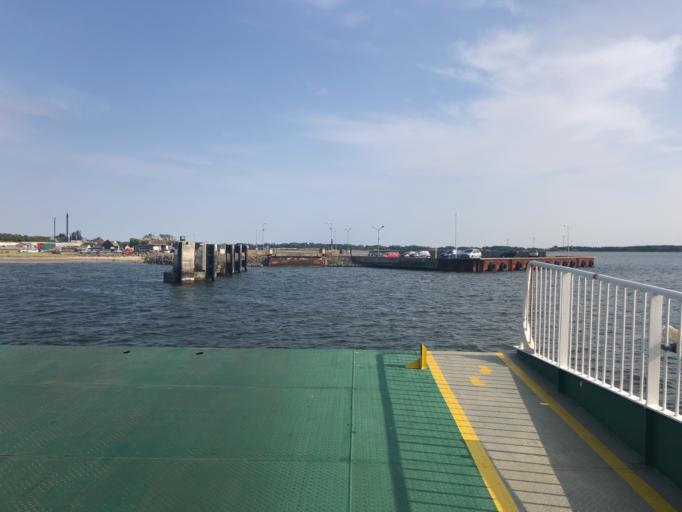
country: DK
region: North Denmark
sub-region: Morso Kommune
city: Nykobing Mors
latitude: 56.8011
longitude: 9.0249
